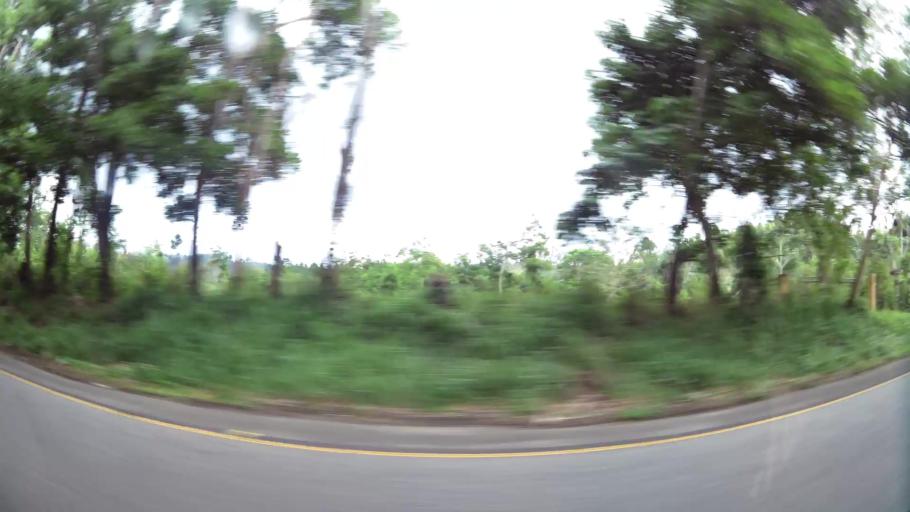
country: DO
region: San Cristobal
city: Villa Altagracia
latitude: 18.7219
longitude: -70.2316
